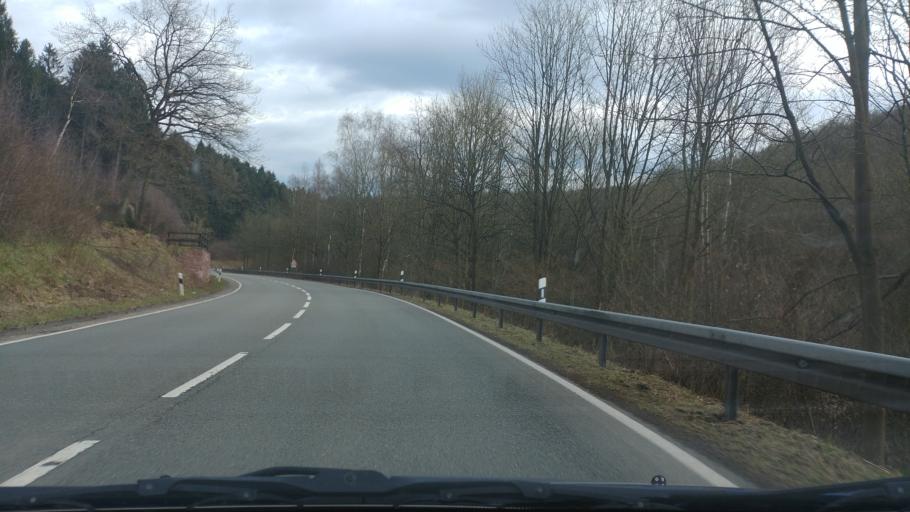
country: DE
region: Lower Saxony
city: Bevern
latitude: 51.8028
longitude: 9.4971
